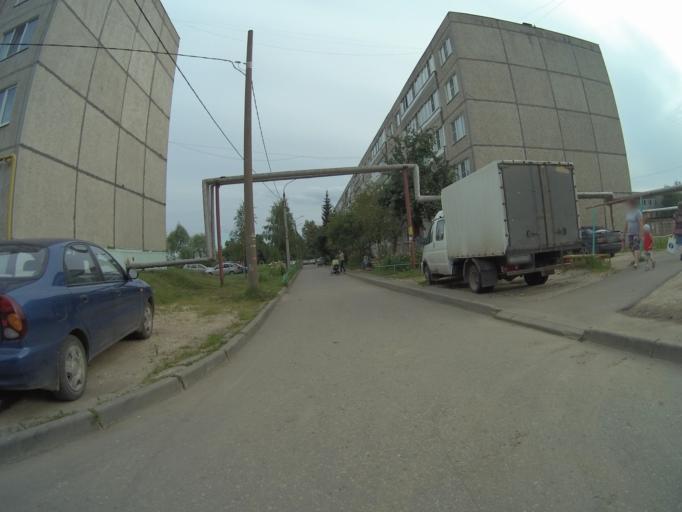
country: RU
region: Vladimir
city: Orgtrud
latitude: 56.2121
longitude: 40.6602
